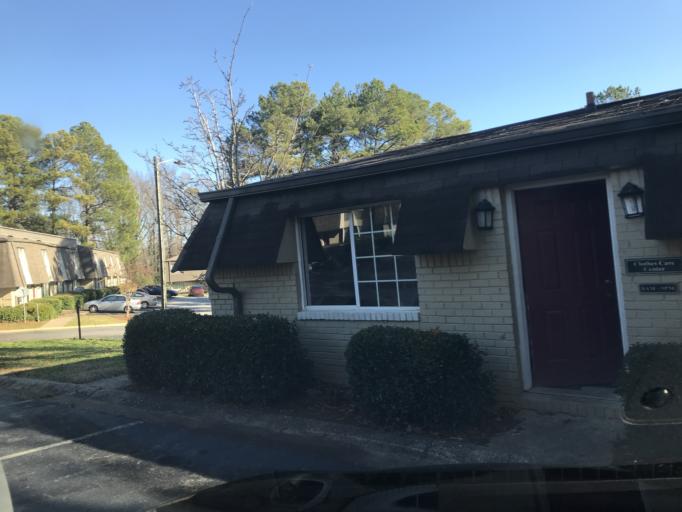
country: US
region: Georgia
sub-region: Clayton County
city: Morrow
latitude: 33.5700
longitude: -84.3671
